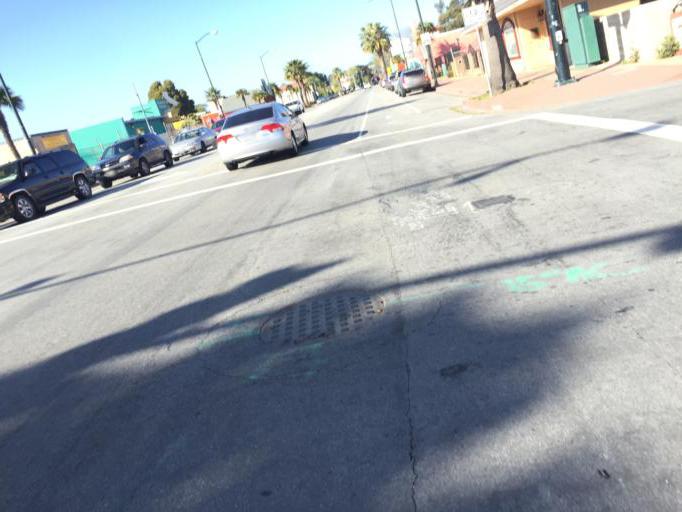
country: US
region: California
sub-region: Contra Costa County
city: San Pablo
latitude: 37.9585
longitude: -122.3470
